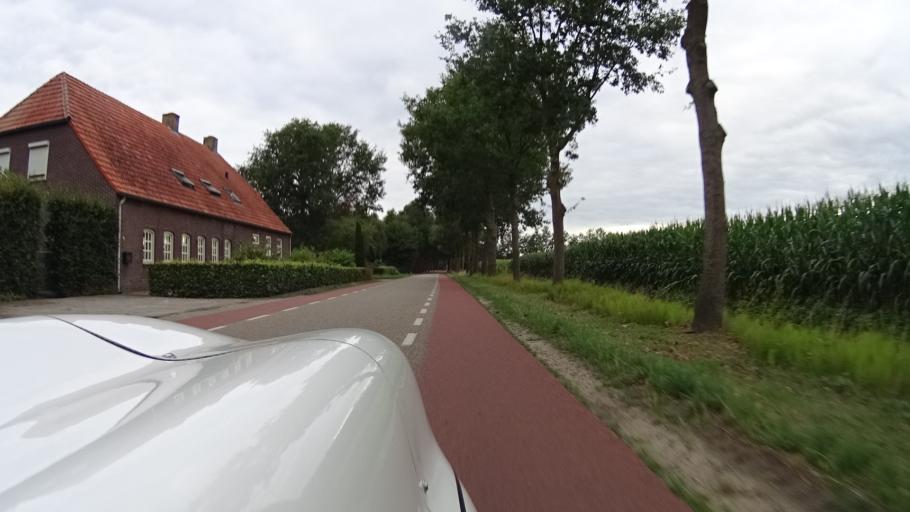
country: NL
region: North Brabant
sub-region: Gemeente Bernheze
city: Loosbroek
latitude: 51.6921
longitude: 5.4653
